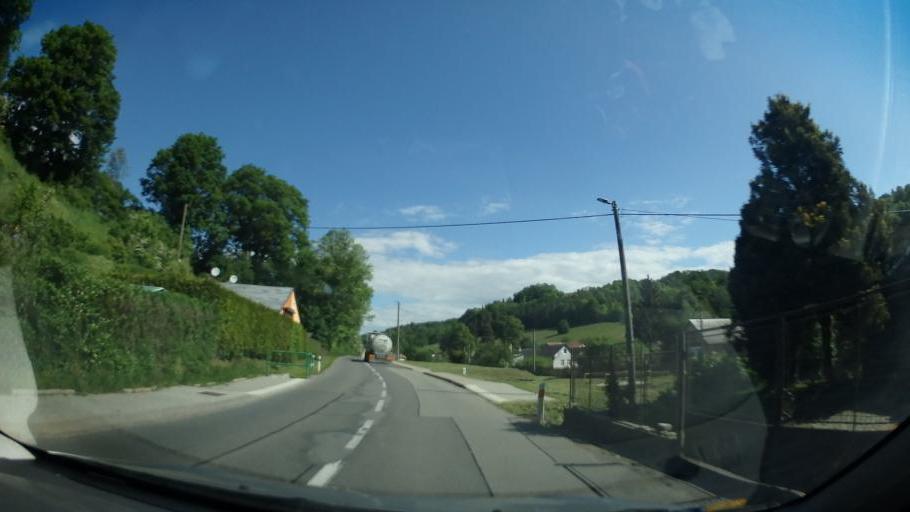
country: CZ
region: Pardubicky
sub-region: Okres Svitavy
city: Moravska Trebova
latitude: 49.7044
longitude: 16.6414
